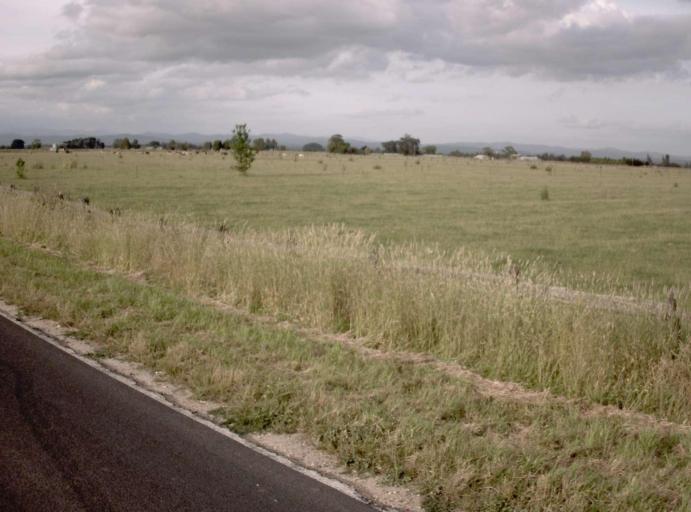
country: AU
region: Victoria
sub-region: Wellington
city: Heyfield
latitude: -37.9009
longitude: 146.9932
